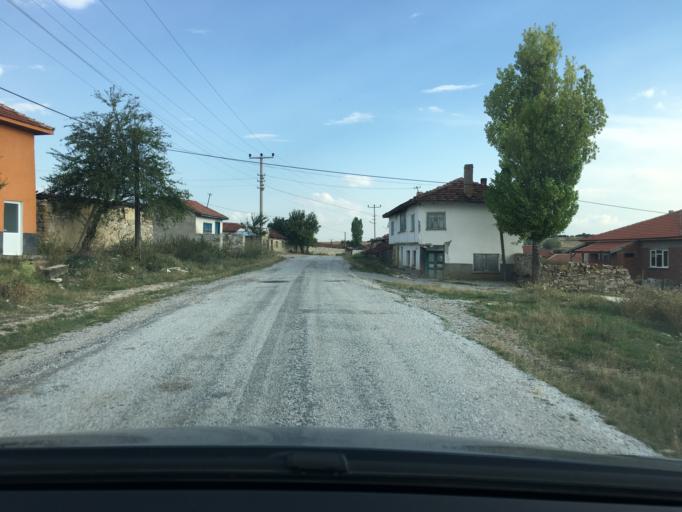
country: TR
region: Eskisehir
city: Kirka
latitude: 39.2756
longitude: 30.6768
